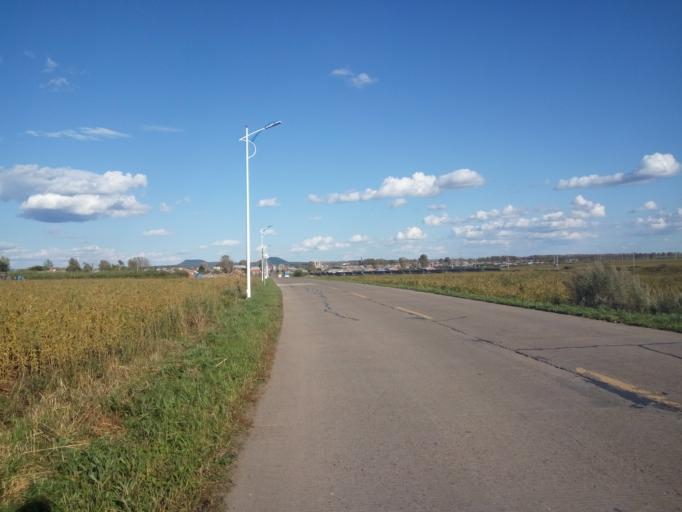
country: CN
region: Heilongjiang Sheng
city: Erjing
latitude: 48.6406
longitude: 126.1246
